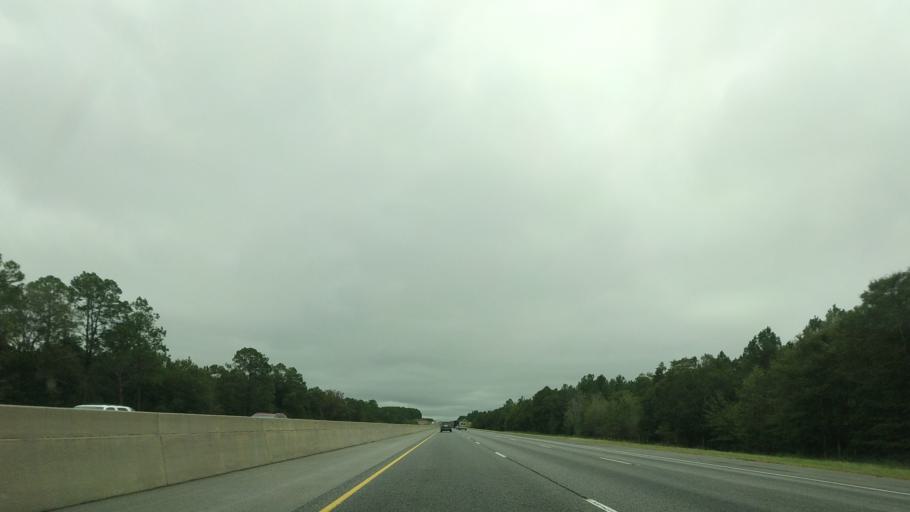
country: US
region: Georgia
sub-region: Turner County
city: Ashburn
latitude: 31.7658
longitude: -83.6747
